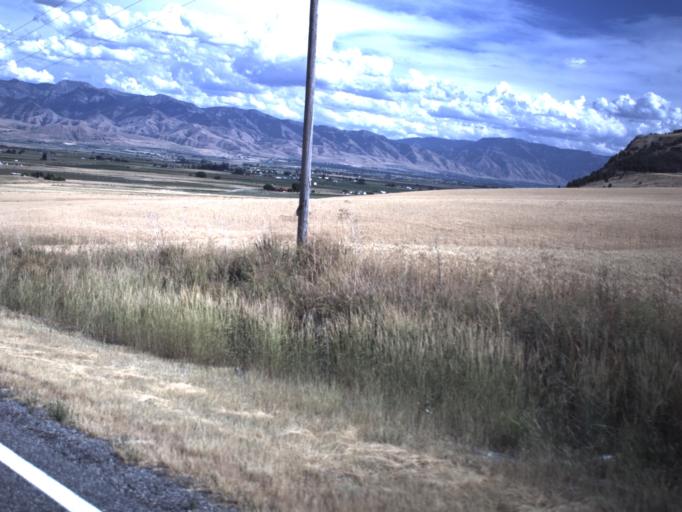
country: US
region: Utah
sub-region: Cache County
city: Lewiston
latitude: 41.9175
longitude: -111.9679
